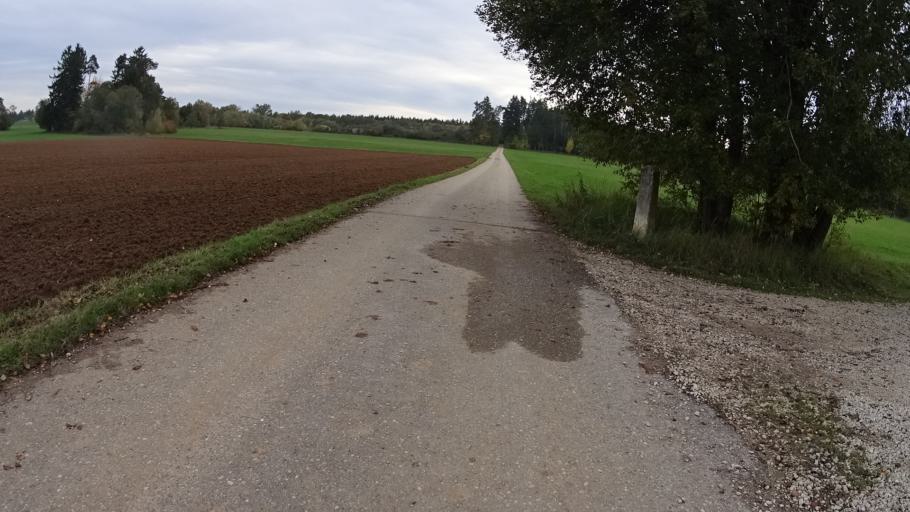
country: DE
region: Bavaria
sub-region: Upper Bavaria
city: Hitzhofen
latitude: 48.8539
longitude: 11.2996
